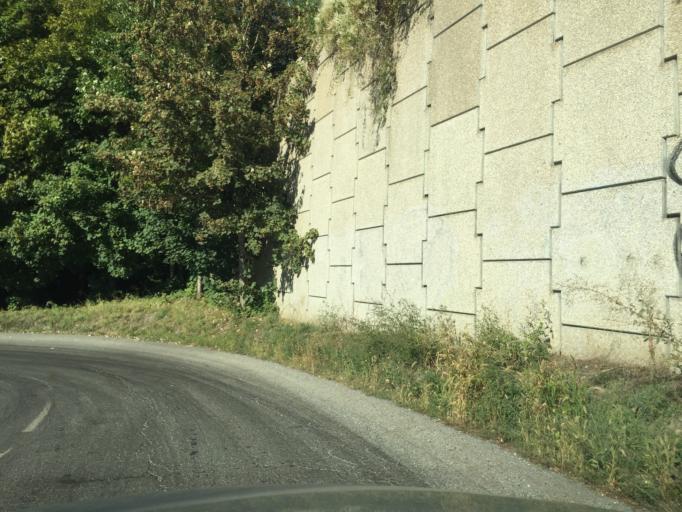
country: FR
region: Rhone-Alpes
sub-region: Departement de la Savoie
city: Macot-la-Plagne
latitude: 45.5680
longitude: 6.7133
